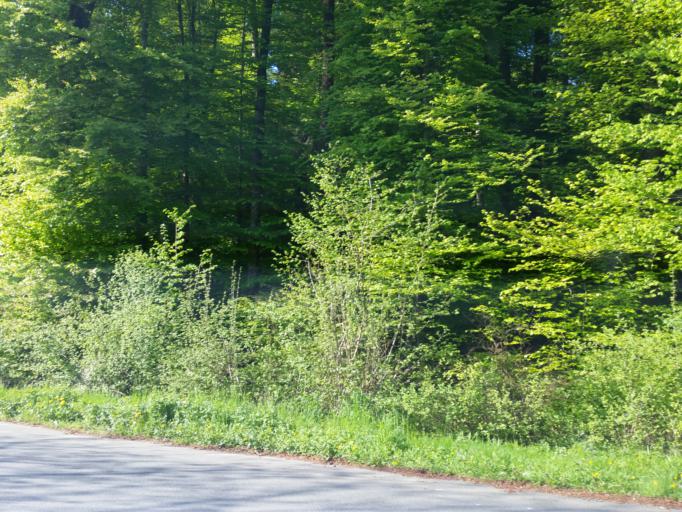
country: DE
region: Baden-Wuerttemberg
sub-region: Freiburg Region
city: Allensbach
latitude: 47.7413
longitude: 9.0376
